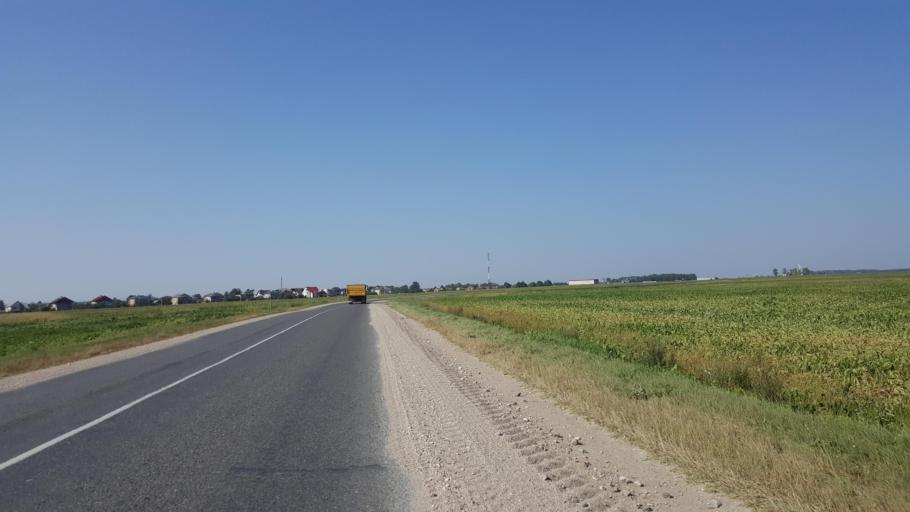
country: BY
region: Brest
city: Kamyanyets
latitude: 52.4144
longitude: 23.6457
